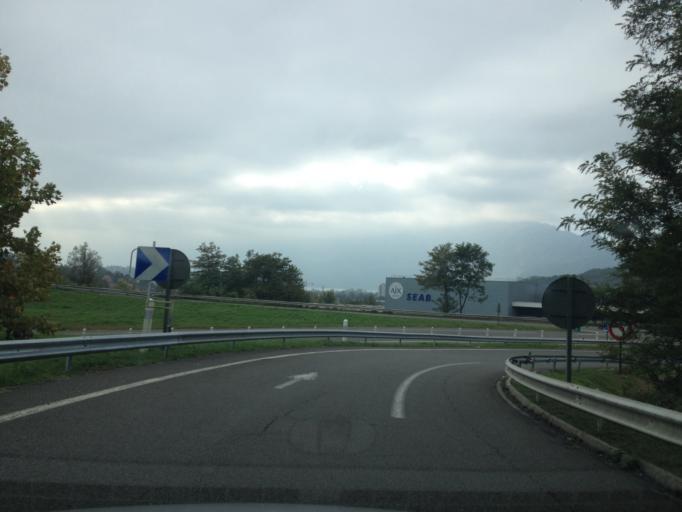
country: FR
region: Rhone-Alpes
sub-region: Departement de la Savoie
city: Gresy-sur-Aix
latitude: 45.7148
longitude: 5.9233
